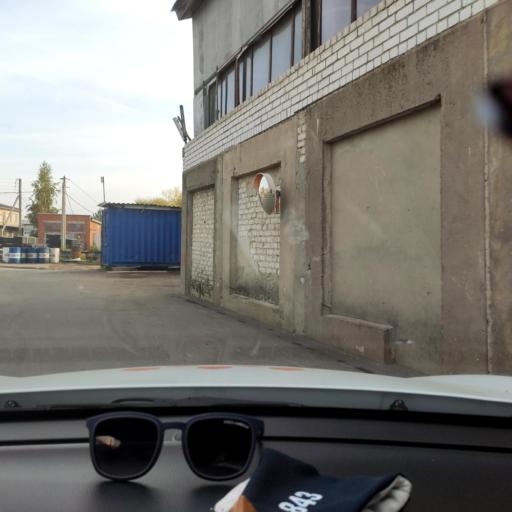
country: RU
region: Tatarstan
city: Staroye Arakchino
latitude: 55.8348
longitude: 49.0291
